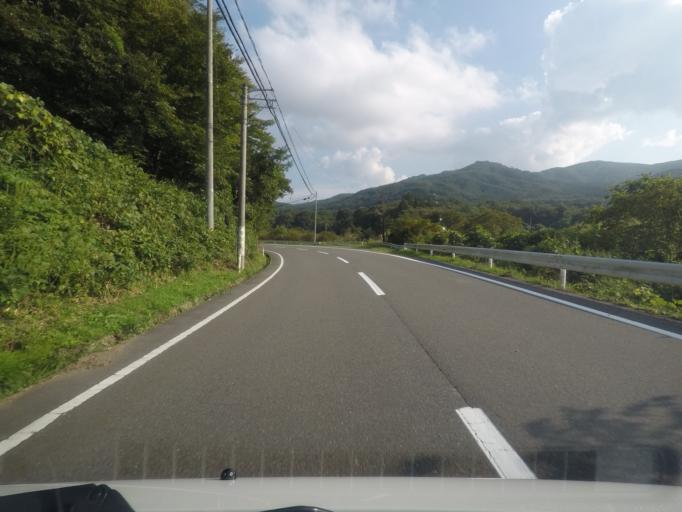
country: JP
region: Fukushima
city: Funehikimachi-funehiki
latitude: 37.5602
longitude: 140.7681
